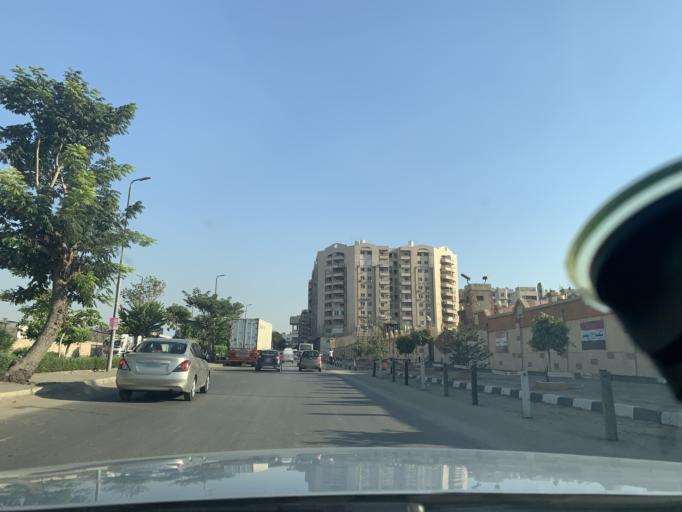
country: EG
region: Muhafazat al Qahirah
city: Cairo
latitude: 30.0400
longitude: 31.3460
